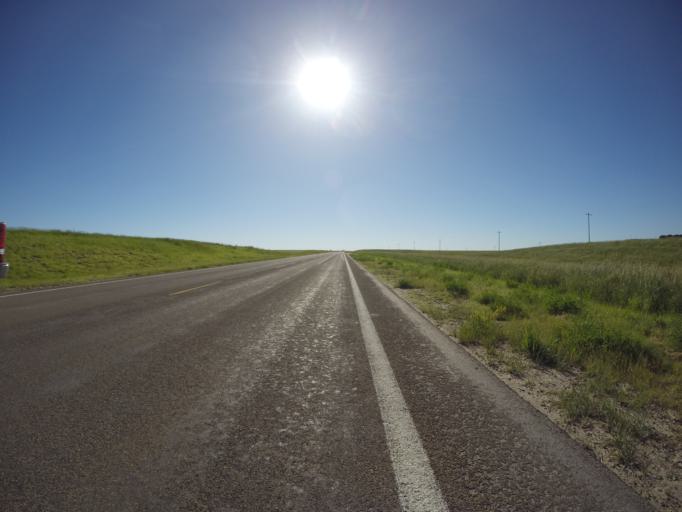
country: US
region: Kansas
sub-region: Norton County
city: Norton
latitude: 39.8281
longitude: -100.0199
